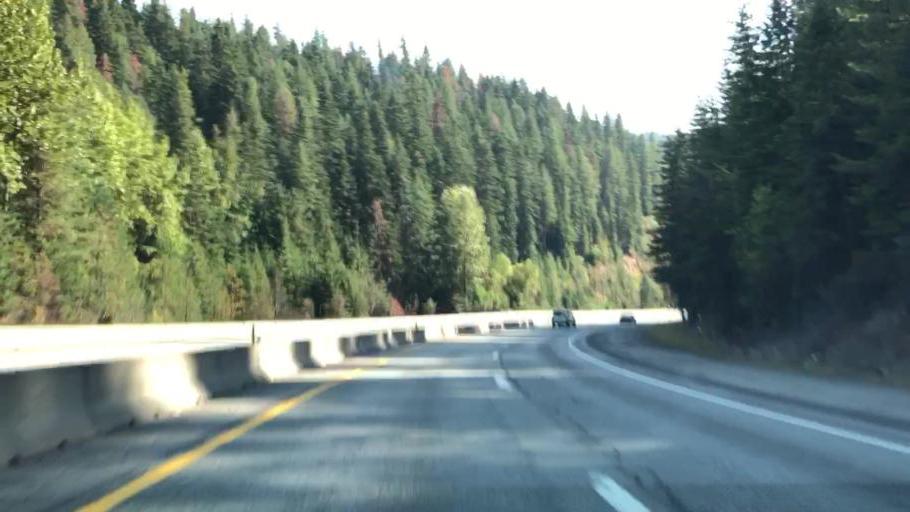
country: US
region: Idaho
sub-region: Shoshone County
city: Pinehurst
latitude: 47.5967
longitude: -116.4926
